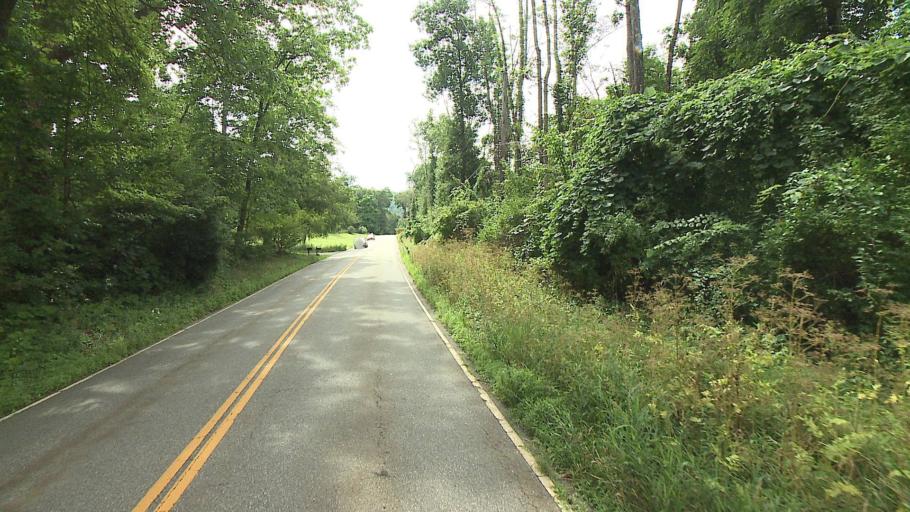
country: US
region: Connecticut
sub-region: Litchfield County
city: Kent
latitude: 41.7447
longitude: -73.5022
